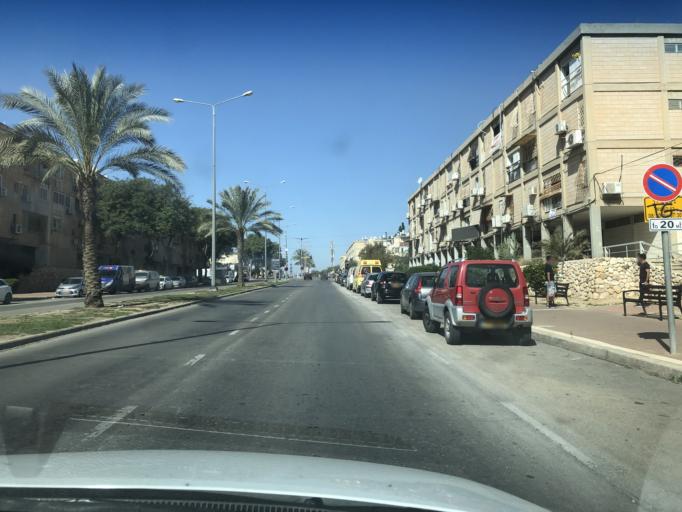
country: IL
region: Southern District
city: Beersheba
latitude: 31.2682
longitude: 34.7982
